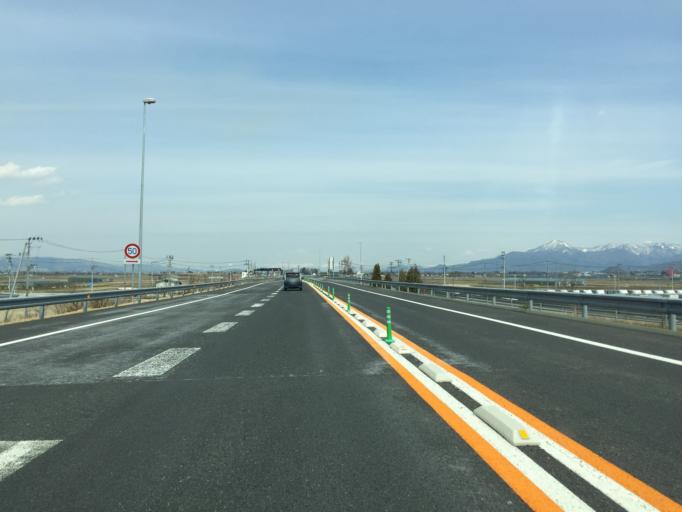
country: JP
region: Yamagata
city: Tendo
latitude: 38.3651
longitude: 140.3462
